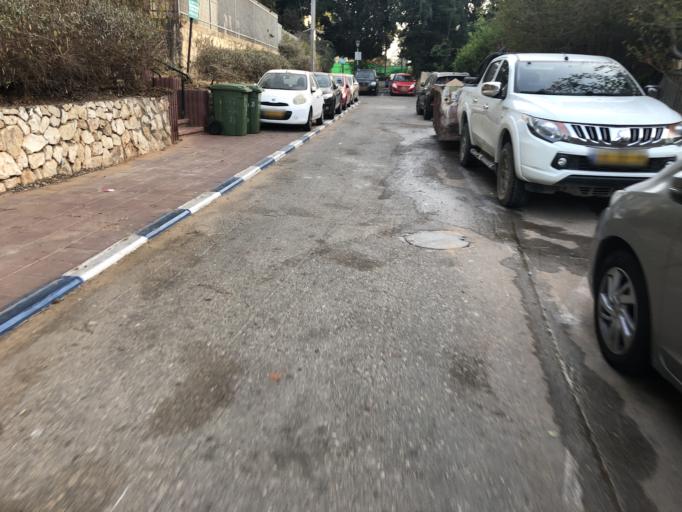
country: IL
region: Tel Aviv
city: Giv`atayim
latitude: 32.0690
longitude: 34.8212
